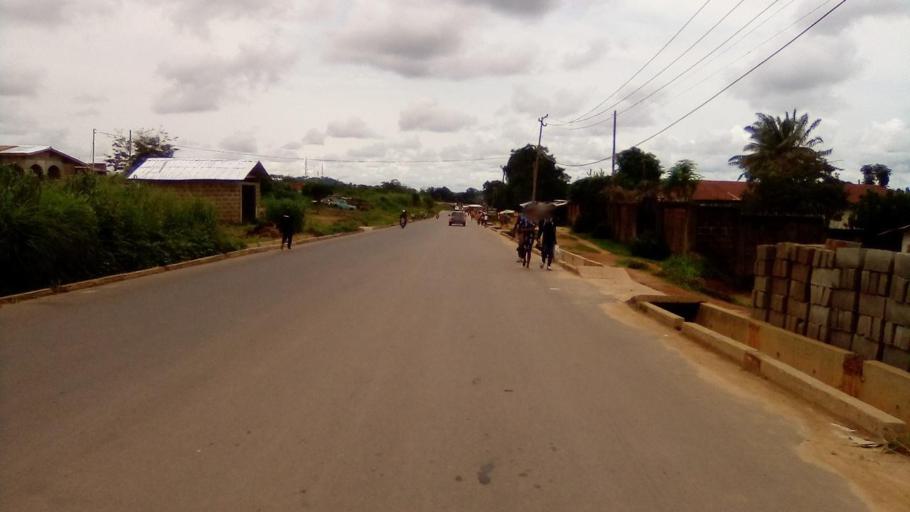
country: SL
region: Southern Province
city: Bo
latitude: 7.9473
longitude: -11.7579
